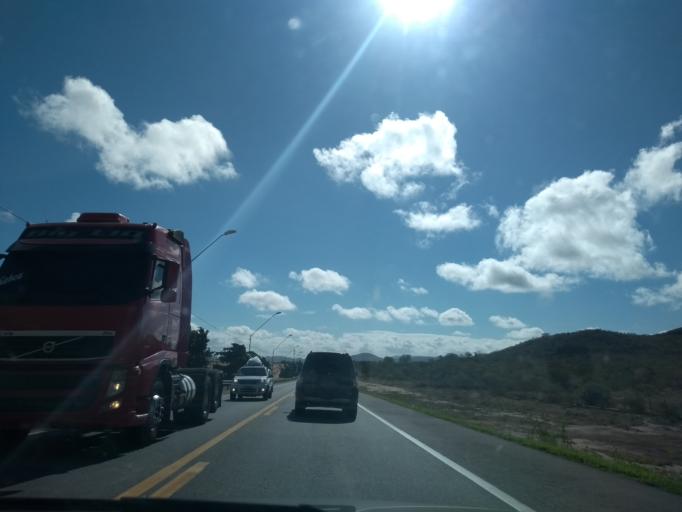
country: BR
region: Bahia
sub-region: Amargosa
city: Amargosa
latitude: -12.8646
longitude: -39.8539
